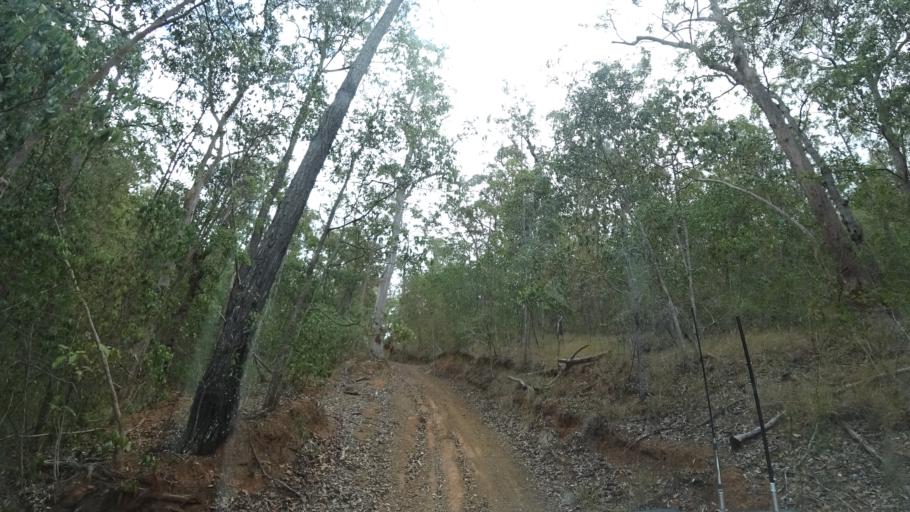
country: AU
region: Queensland
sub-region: Moreton Bay
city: Highvale
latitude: -27.4261
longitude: 152.7447
